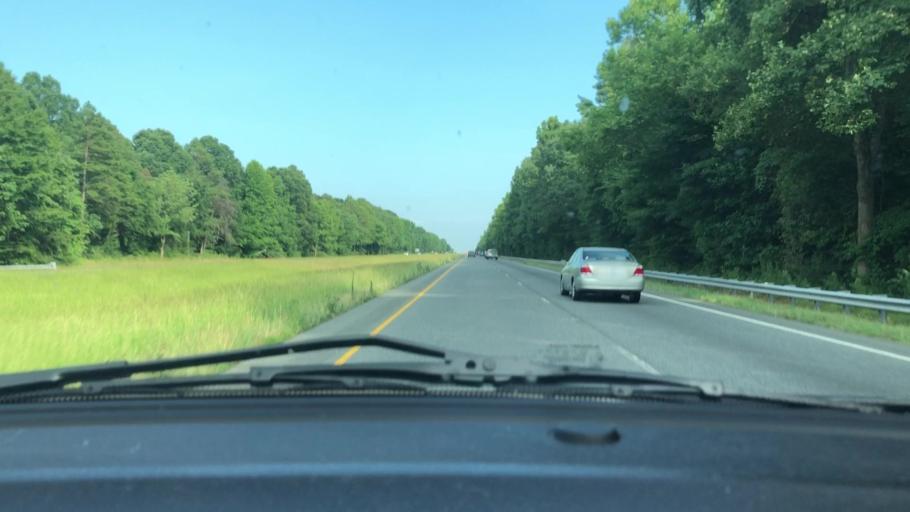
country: US
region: North Carolina
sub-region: Randolph County
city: Liberty
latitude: 35.8397
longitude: -79.5961
